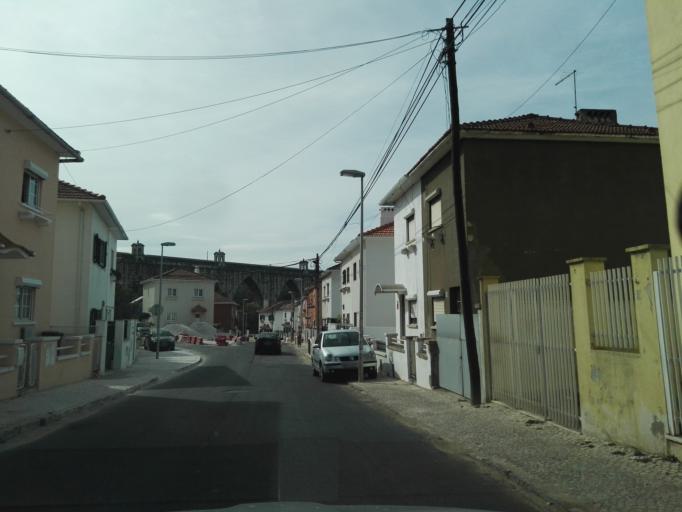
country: PT
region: Lisbon
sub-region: Lisbon
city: Lisbon
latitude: 38.7294
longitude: -9.1665
